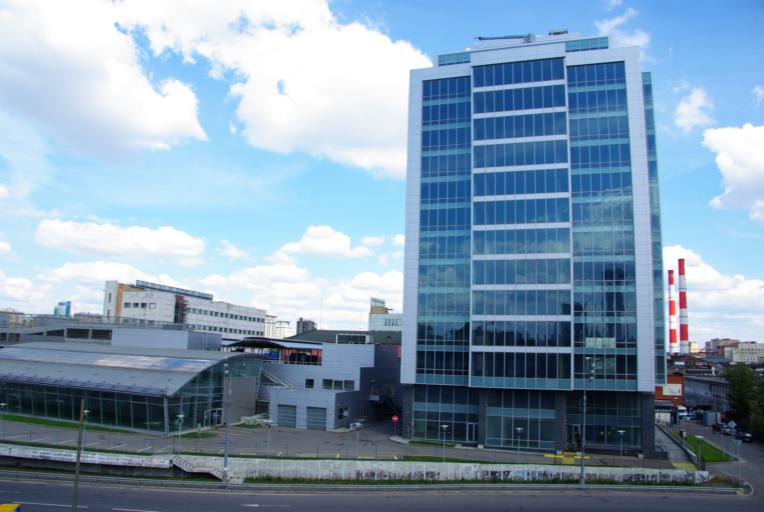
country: RU
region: Moscow
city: Luzhniki
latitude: 55.7316
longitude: 37.5445
